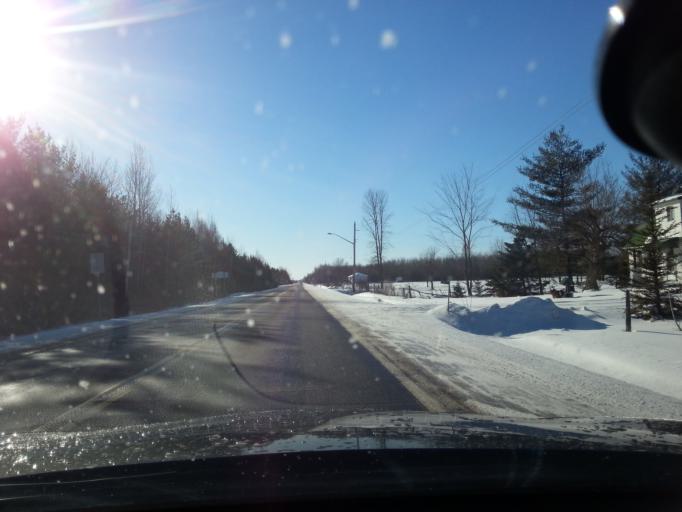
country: CA
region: Ontario
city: Ottawa
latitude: 45.3198
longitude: -75.4738
